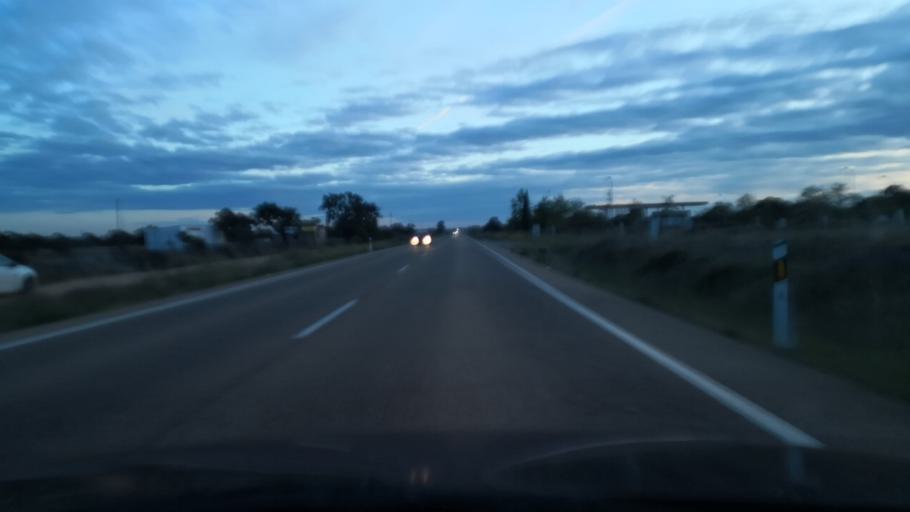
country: ES
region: Extremadura
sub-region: Provincia de Badajoz
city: Villar del Rey
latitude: 38.9948
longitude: -6.8711
